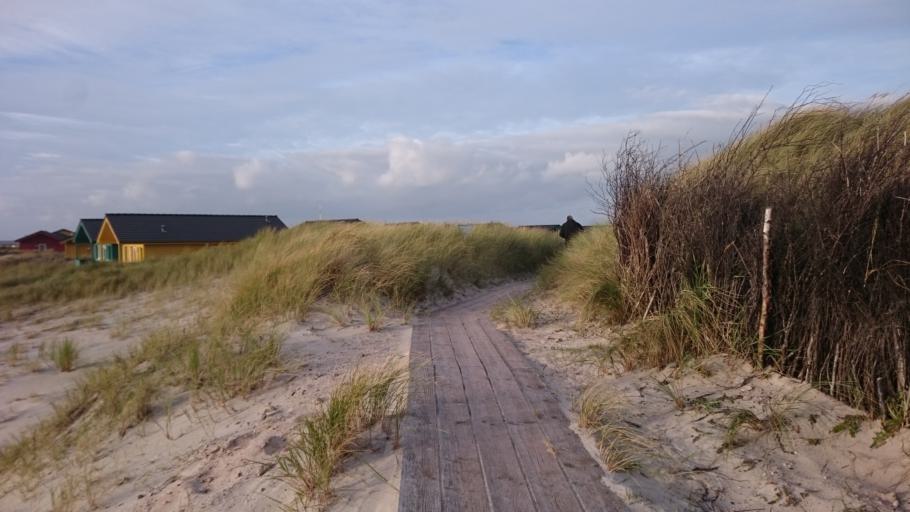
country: DE
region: Schleswig-Holstein
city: Helgoland
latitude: 54.1827
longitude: 7.9071
